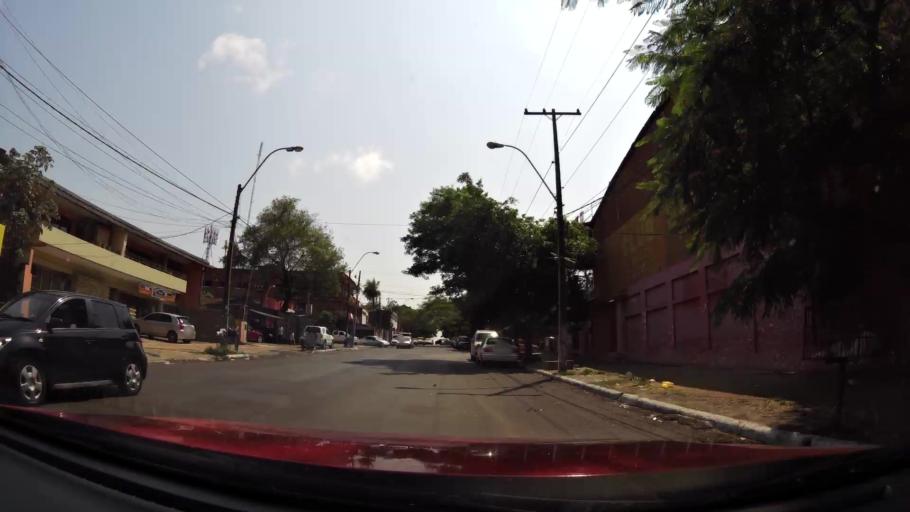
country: PY
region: Asuncion
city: Asuncion
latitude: -25.2913
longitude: -57.6503
